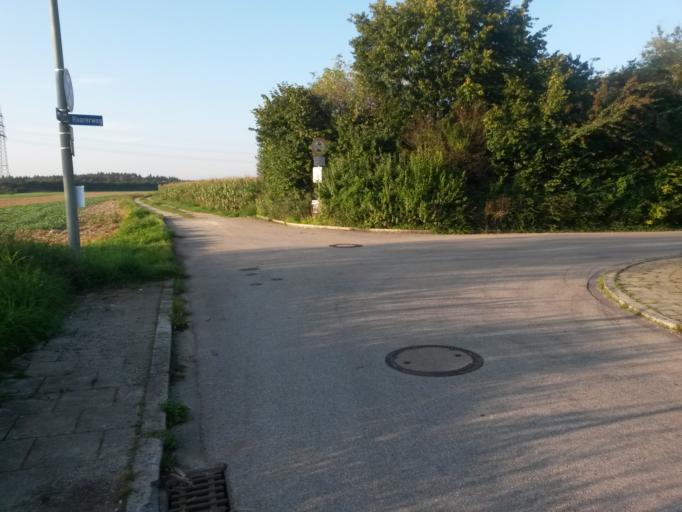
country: DE
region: Bavaria
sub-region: Upper Bavaria
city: Grasbrunn
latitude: 48.0822
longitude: 11.7440
